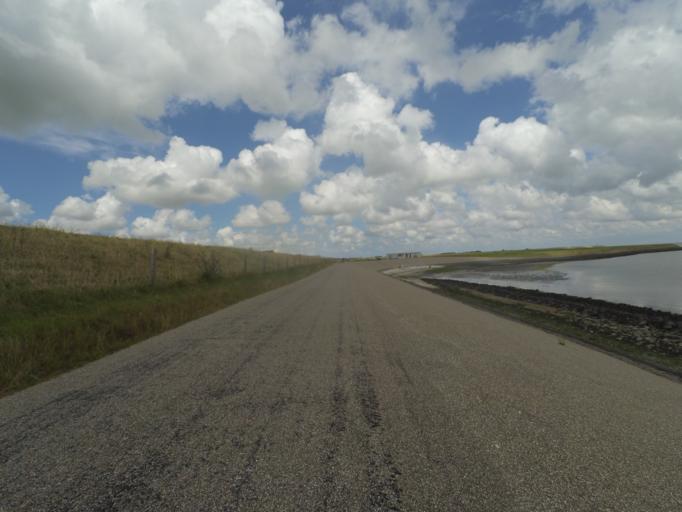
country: NL
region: North Holland
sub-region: Gemeente Texel
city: Den Burg
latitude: 53.0638
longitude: 4.8725
